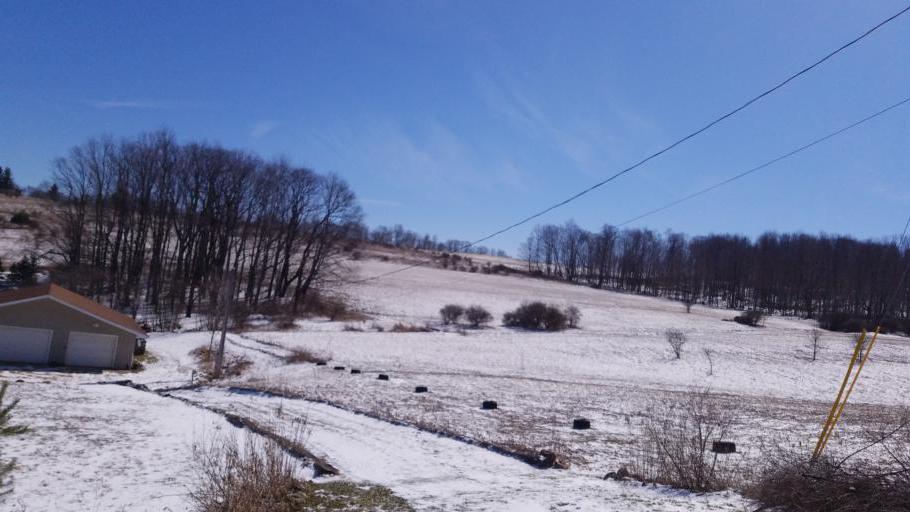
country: US
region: New York
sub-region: Allegany County
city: Andover
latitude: 42.0258
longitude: -77.7603
